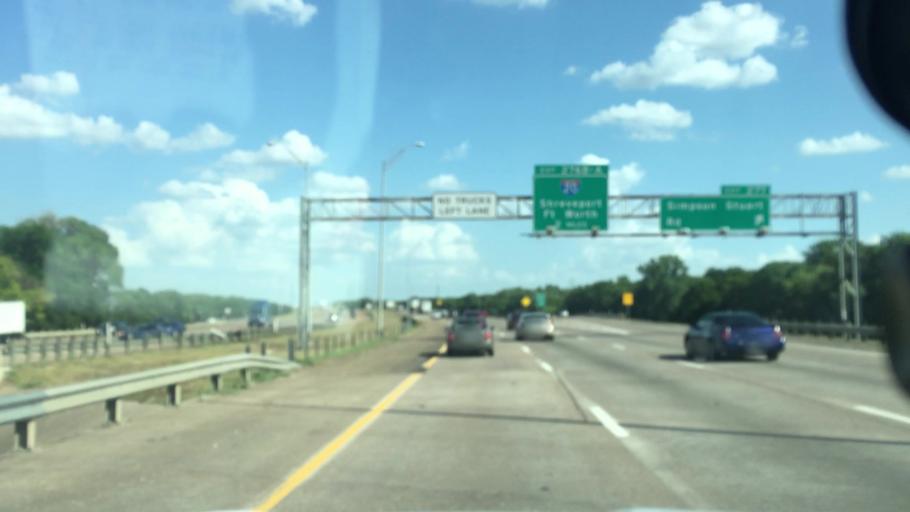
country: US
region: Texas
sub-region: Dallas County
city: Hutchins
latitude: 32.6853
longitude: -96.7472
